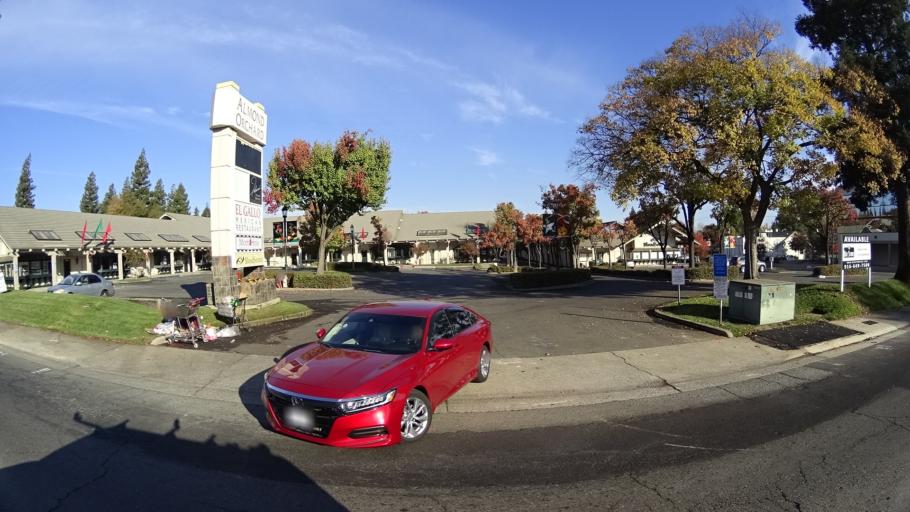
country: US
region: California
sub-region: Sacramento County
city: Fair Oaks
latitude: 38.6641
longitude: -121.2632
